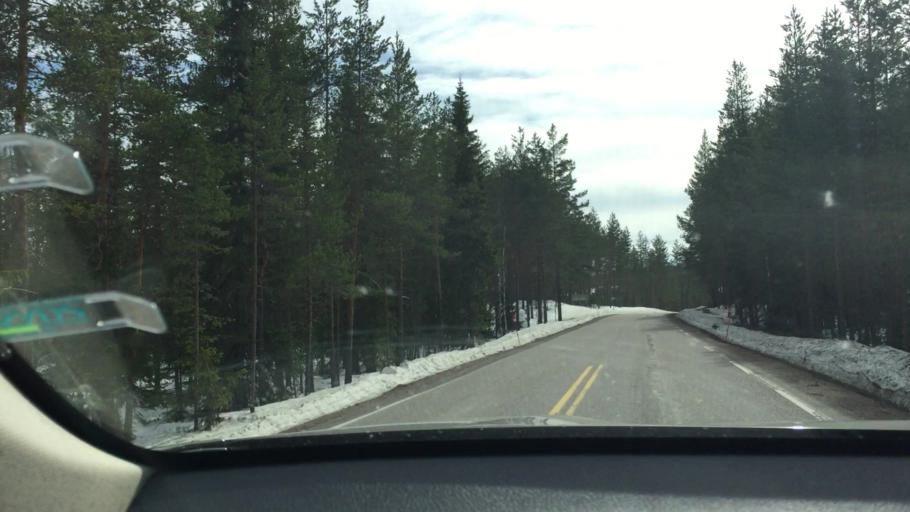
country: NO
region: Hedmark
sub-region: Trysil
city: Innbygda
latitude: 61.0747
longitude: 12.5734
